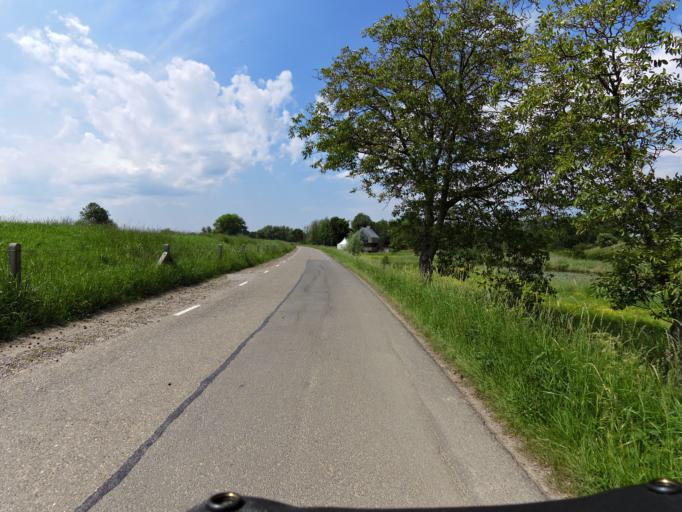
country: NL
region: North Brabant
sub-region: Gemeente Woudrichem
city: Woudrichem
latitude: 51.7915
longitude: 5.0625
